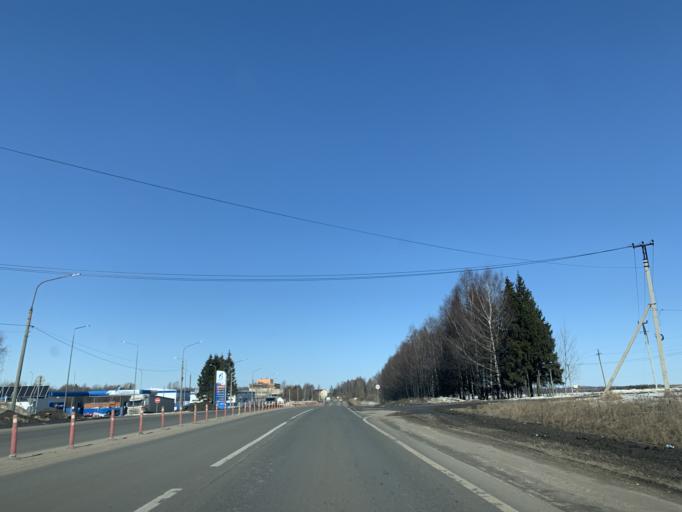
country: RU
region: Jaroslavl
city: Tutayev
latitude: 57.8483
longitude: 39.5474
